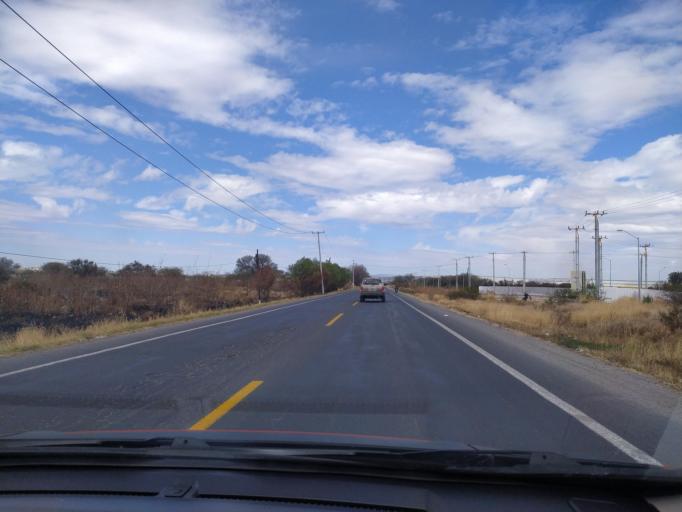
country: LA
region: Oudomxai
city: Muang La
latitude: 20.9986
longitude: 101.8329
